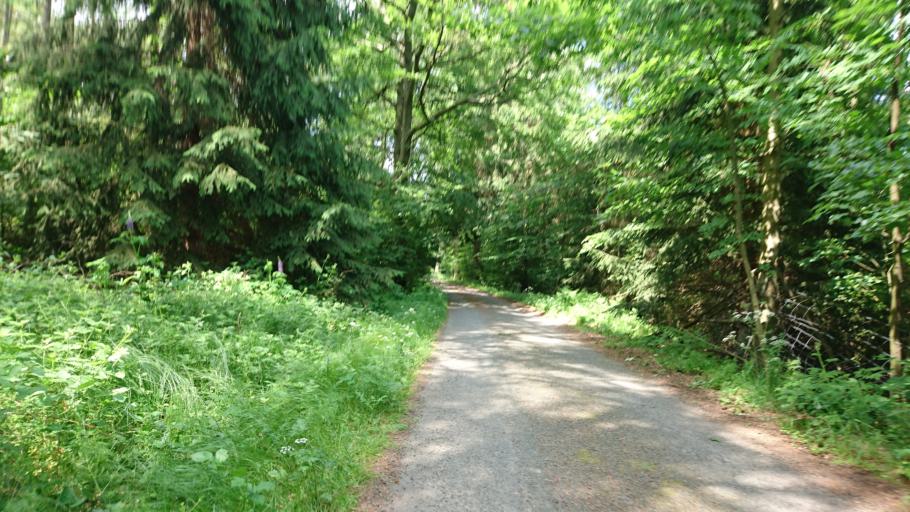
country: DE
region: Saxony
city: Bad Schandau
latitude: 50.8619
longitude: 14.1814
